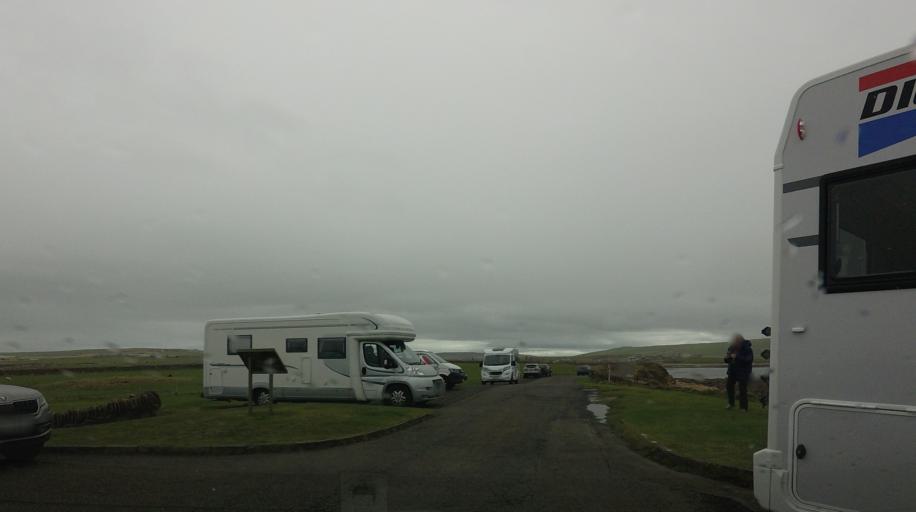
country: GB
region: Scotland
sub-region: Orkney Islands
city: Stromness
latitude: 59.1352
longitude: -3.3247
